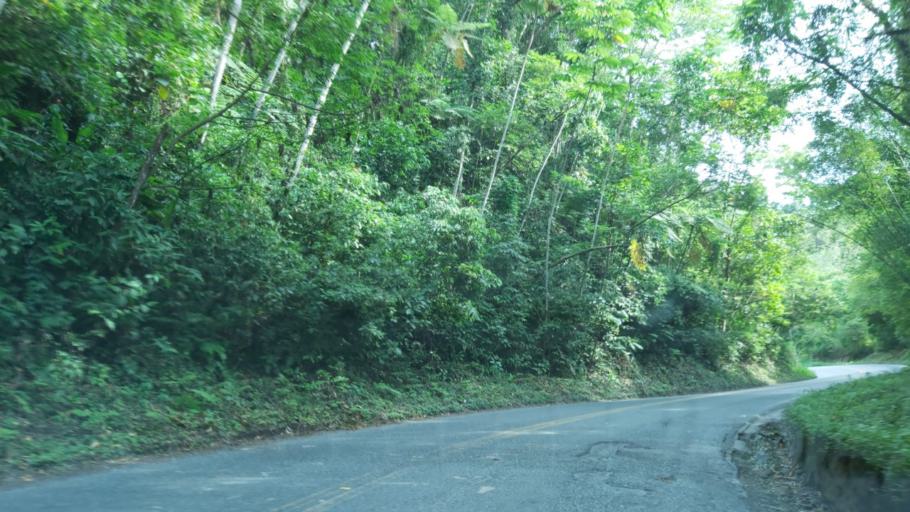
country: BR
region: Sao Paulo
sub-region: Juquia
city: Juquia
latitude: -24.1093
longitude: -47.6266
